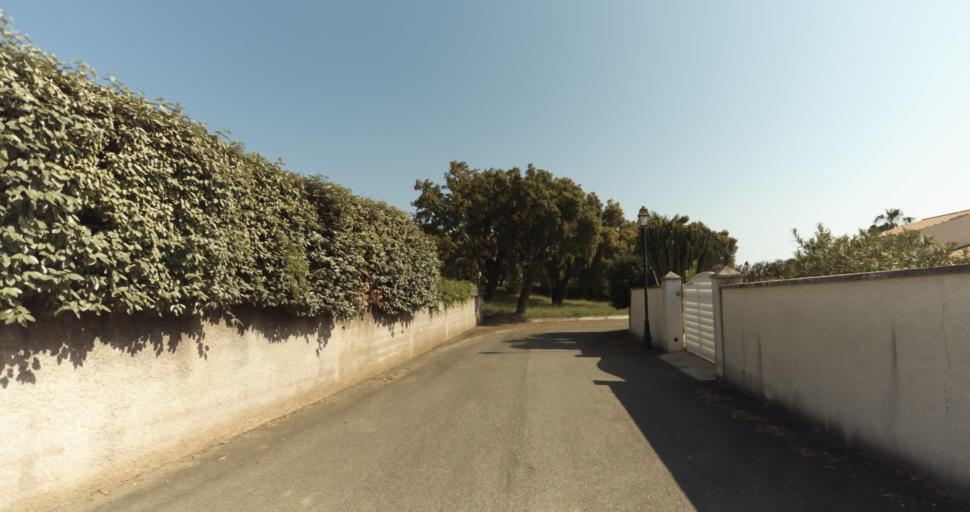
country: FR
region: Corsica
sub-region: Departement de la Haute-Corse
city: Biguglia
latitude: 42.6223
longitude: 9.4314
